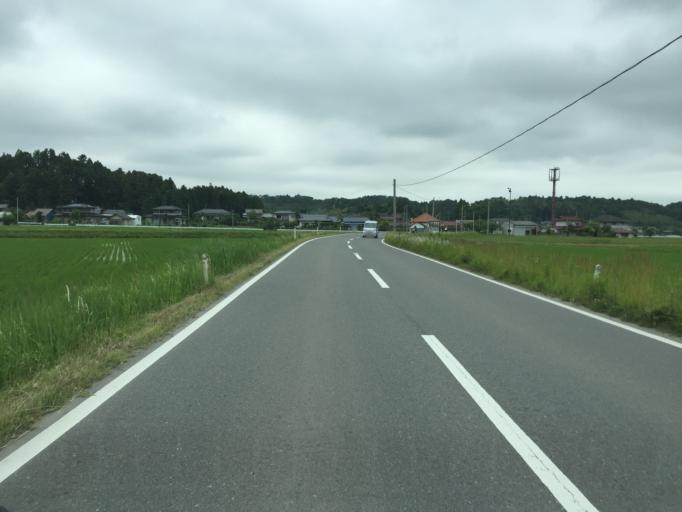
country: JP
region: Miyagi
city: Marumori
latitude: 37.7494
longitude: 140.9153
